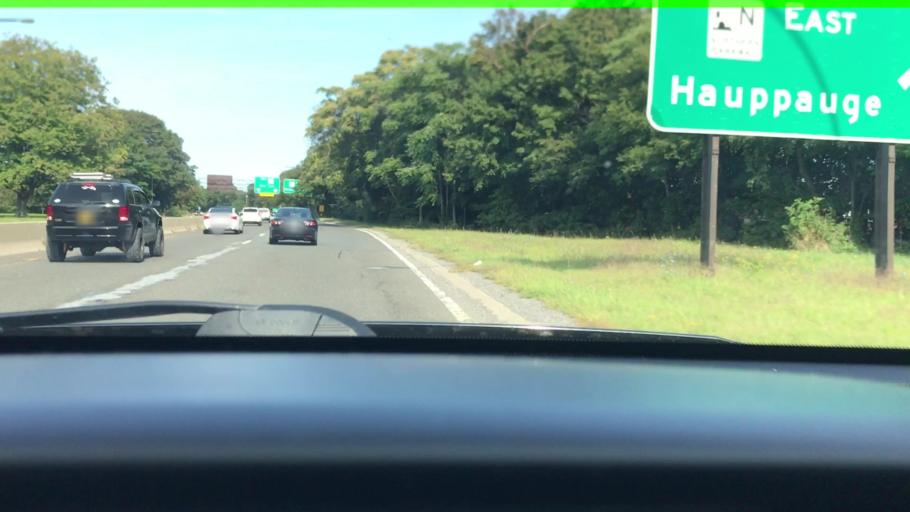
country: US
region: New York
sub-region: Nassau County
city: New Cassel
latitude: 40.7691
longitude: -73.5621
